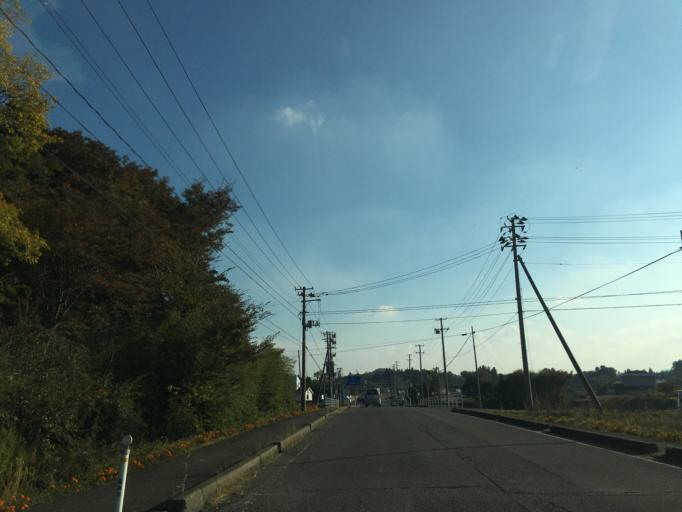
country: JP
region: Fukushima
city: Koriyama
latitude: 37.4000
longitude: 140.2685
